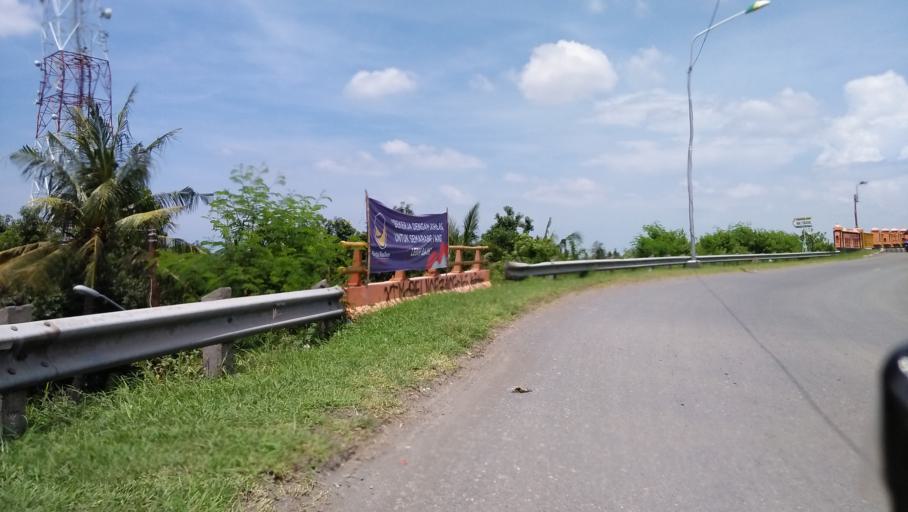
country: ID
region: Central Java
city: Semarang
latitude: -6.9845
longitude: 110.4742
